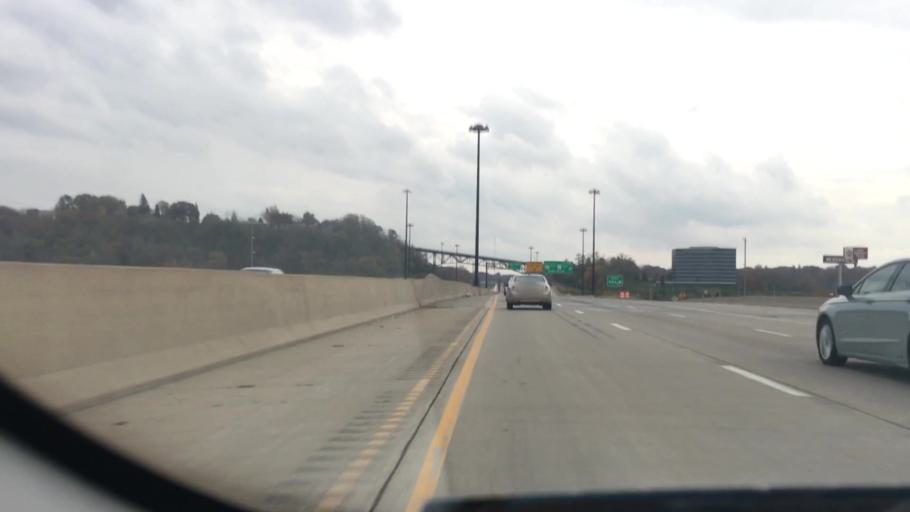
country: US
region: Illinois
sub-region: Tazewell County
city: East Peoria
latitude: 40.6737
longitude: -89.5762
